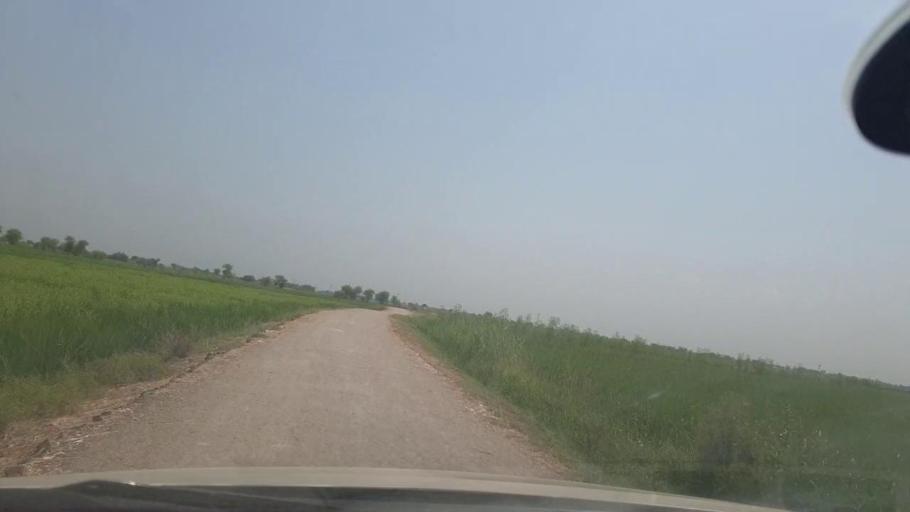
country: PK
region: Sindh
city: Jacobabad
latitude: 28.1705
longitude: 68.3908
